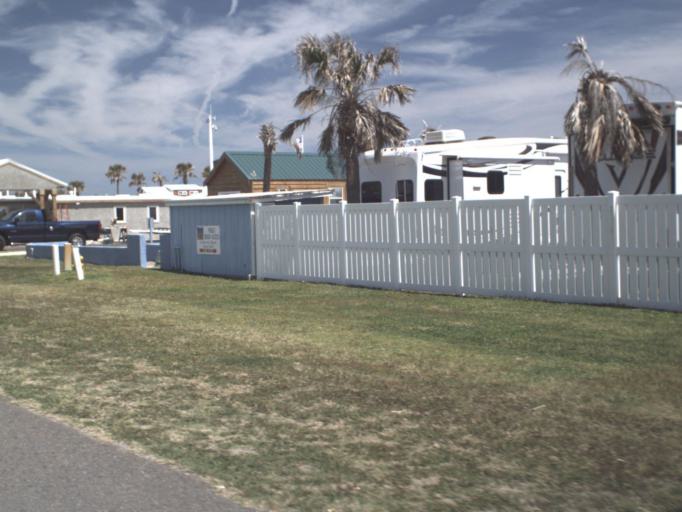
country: US
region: Florida
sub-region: Flagler County
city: Flagler Beach
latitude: 29.5210
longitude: -81.1475
